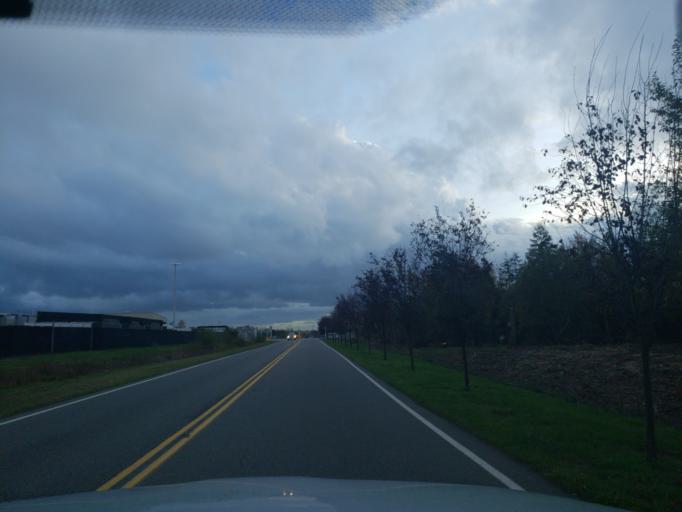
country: US
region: Washington
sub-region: Snohomish County
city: Mukilteo
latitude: 47.9299
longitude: -122.2847
